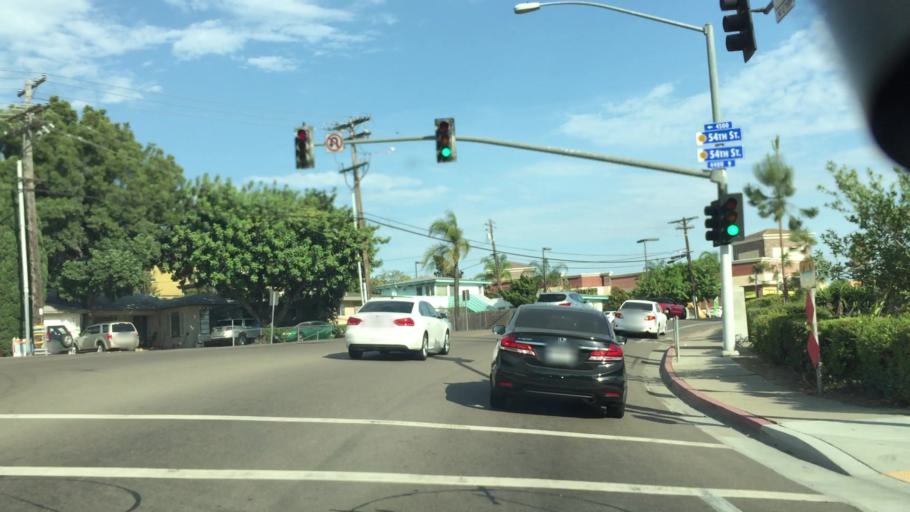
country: US
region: California
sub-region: San Diego County
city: Lemon Grove
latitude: 32.7591
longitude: -117.0798
